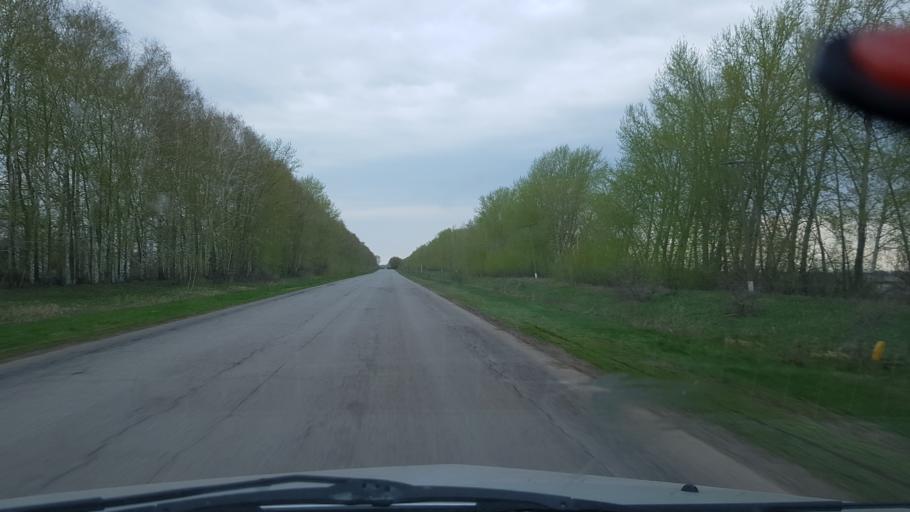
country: RU
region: Samara
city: Podstepki
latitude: 53.6640
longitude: 49.1846
